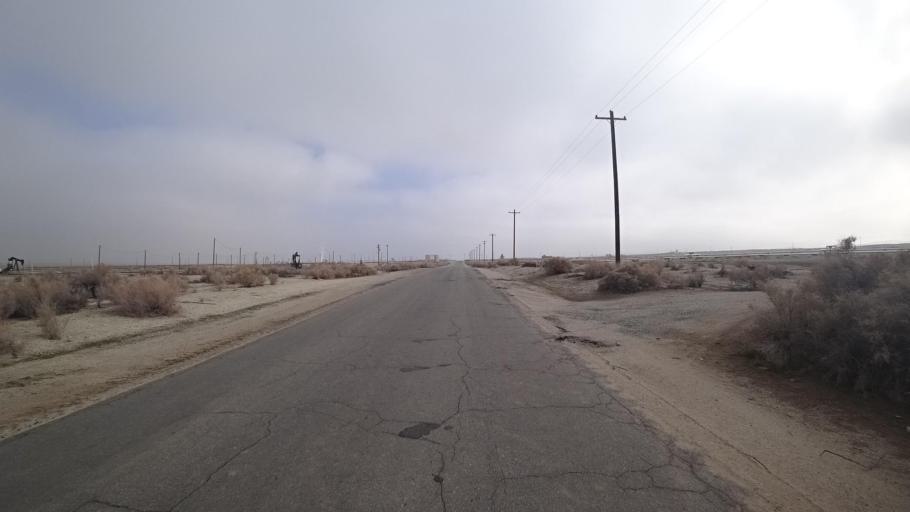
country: US
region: California
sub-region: Kern County
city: Maricopa
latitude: 35.0352
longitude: -119.3538
